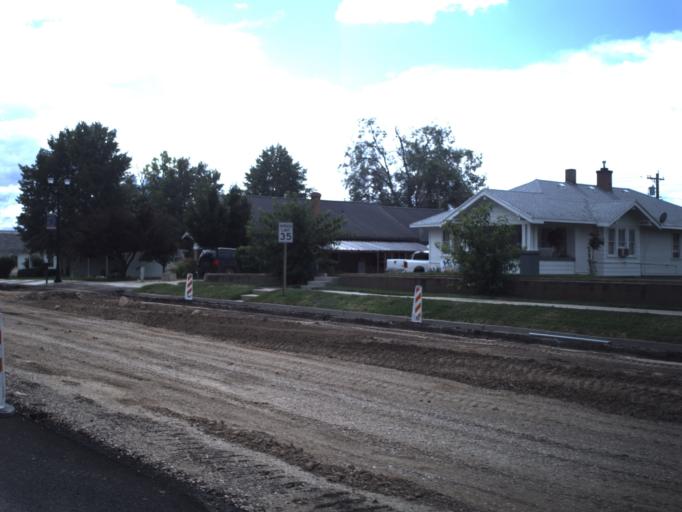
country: US
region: Utah
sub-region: Millard County
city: Fillmore
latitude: 38.9639
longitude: -112.3236
